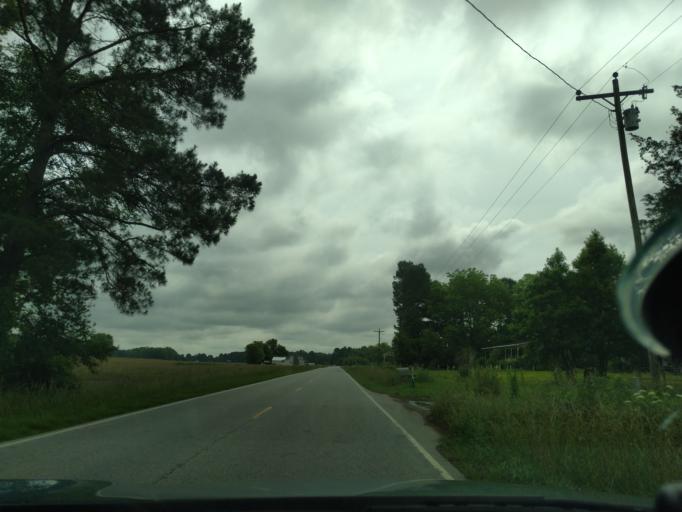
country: US
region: North Carolina
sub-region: Washington County
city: Plymouth
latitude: 35.8548
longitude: -76.7258
